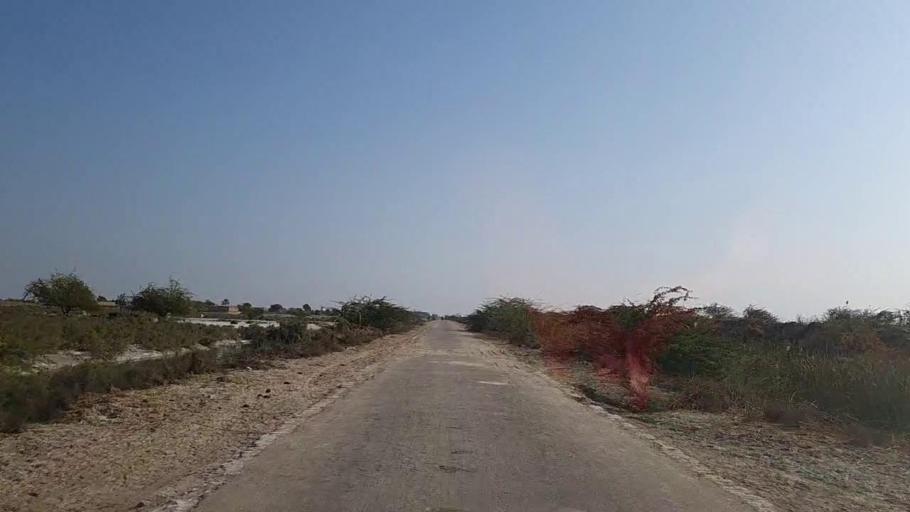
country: PK
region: Sindh
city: Tando Mittha Khan
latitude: 25.9358
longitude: 69.0587
